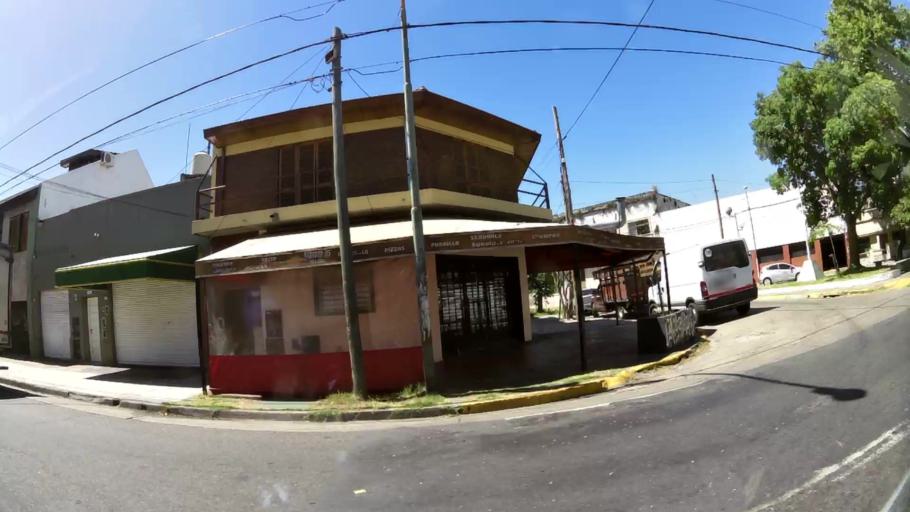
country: AR
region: Buenos Aires
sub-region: Partido de General San Martin
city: General San Martin
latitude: -34.5941
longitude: -58.5370
